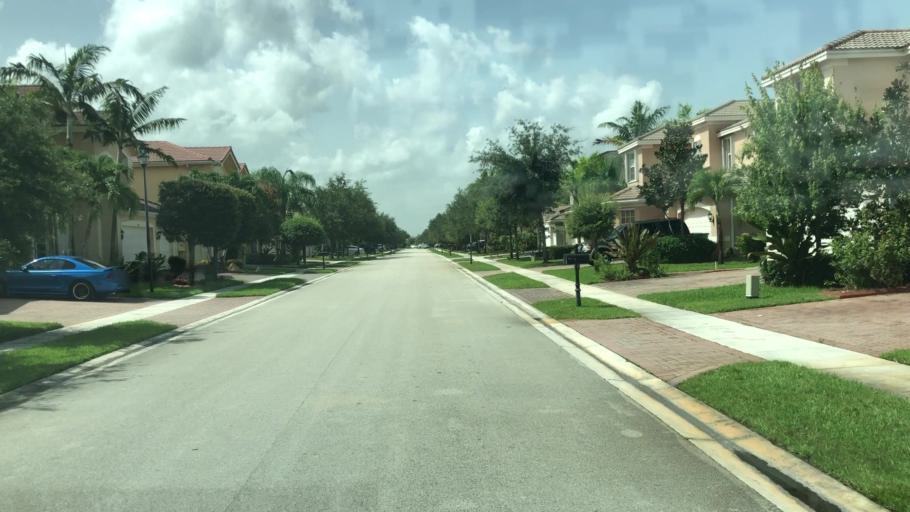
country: US
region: Florida
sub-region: Miami-Dade County
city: Palm Springs North
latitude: 25.9690
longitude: -80.3839
